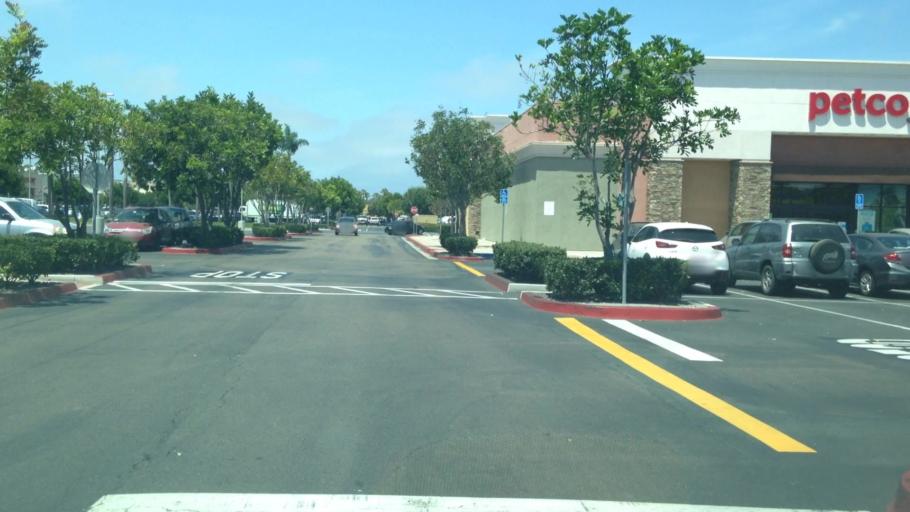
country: US
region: California
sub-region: San Diego County
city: San Diego
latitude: 32.7528
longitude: -117.2106
